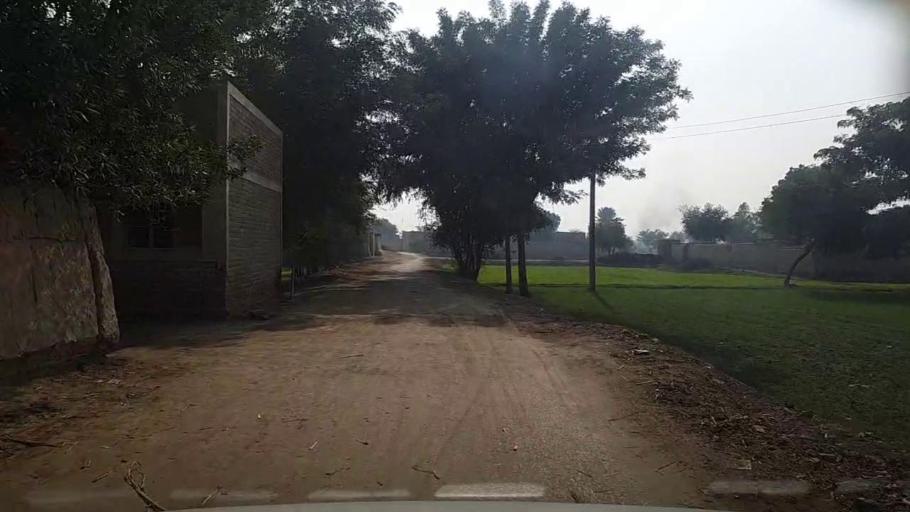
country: PK
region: Sindh
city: Setharja Old
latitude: 27.1260
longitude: 68.5157
